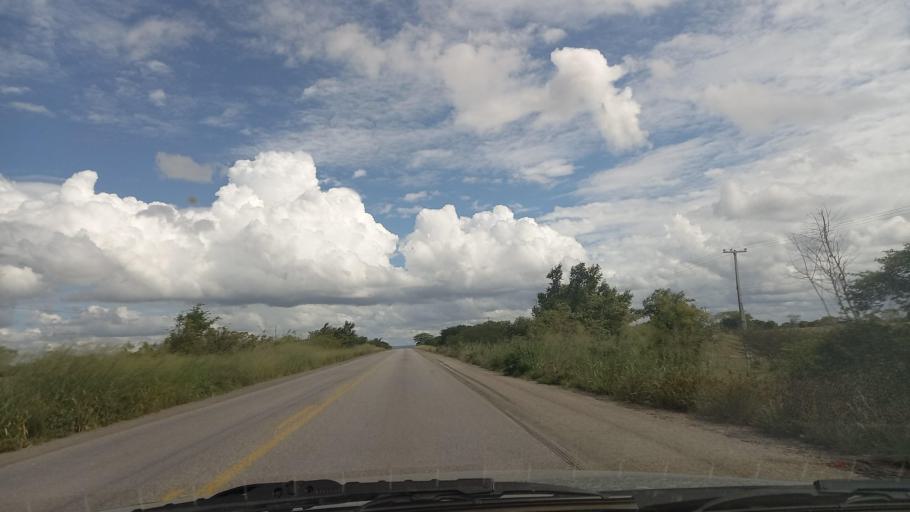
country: BR
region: Pernambuco
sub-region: Cachoeirinha
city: Cachoeirinha
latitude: -8.4418
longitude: -36.2063
